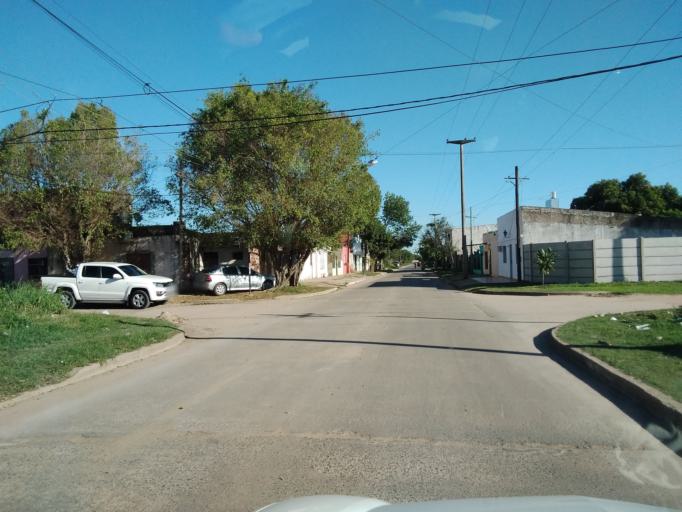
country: AR
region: Corrientes
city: Corrientes
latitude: -27.4693
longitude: -58.7910
